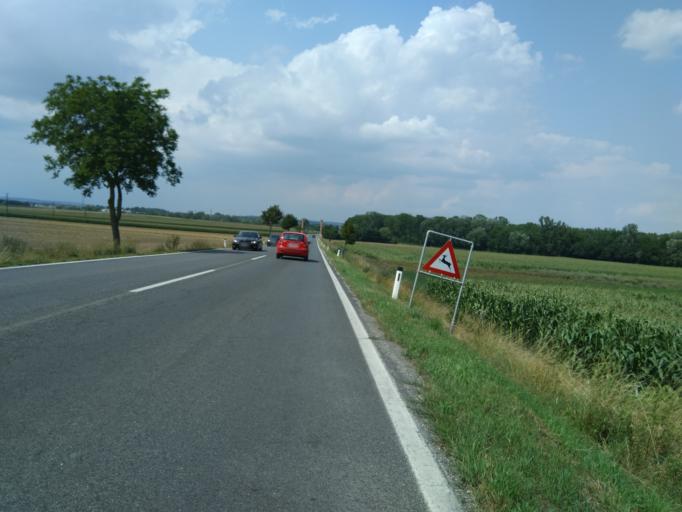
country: AT
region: Lower Austria
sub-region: Politischer Bezirk Ganserndorf
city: Ganserndorf
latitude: 48.3450
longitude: 16.7137
